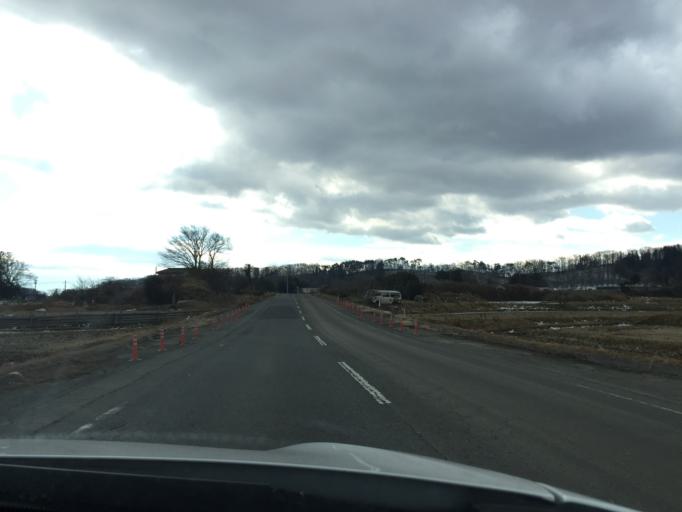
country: JP
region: Fukushima
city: Koriyama
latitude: 37.4039
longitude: 140.3071
